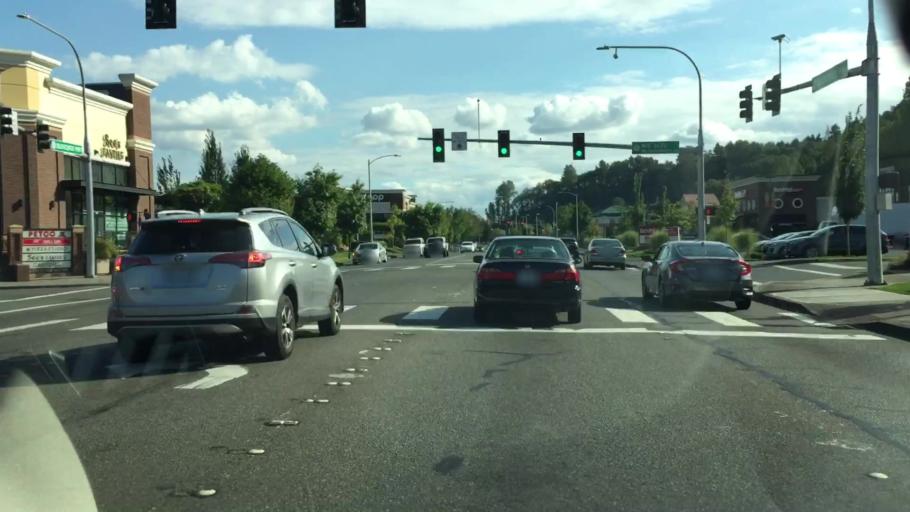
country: US
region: Washington
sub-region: King County
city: Tukwila
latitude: 47.4506
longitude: -122.2625
